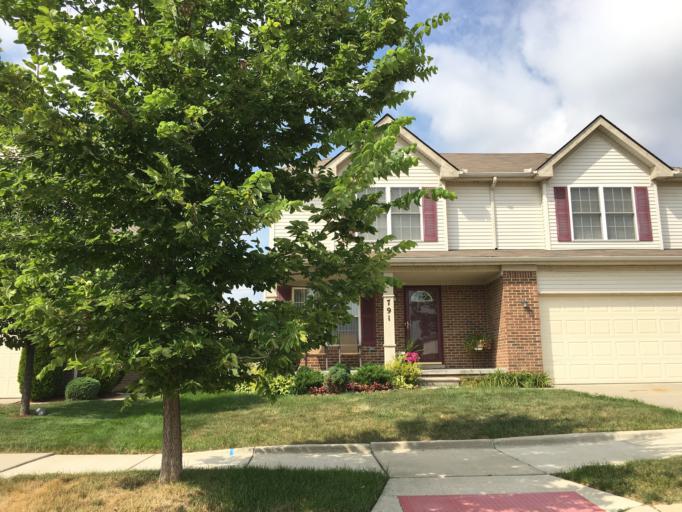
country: US
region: Michigan
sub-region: Wayne County
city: Grosse Pointe Park
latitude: 42.3627
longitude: -82.9752
